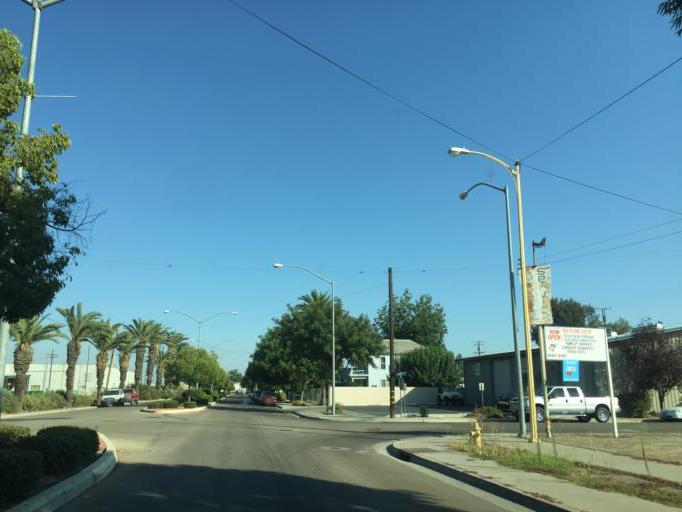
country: US
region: California
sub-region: Fresno County
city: Kingsburg
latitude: 36.5129
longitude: -119.5536
